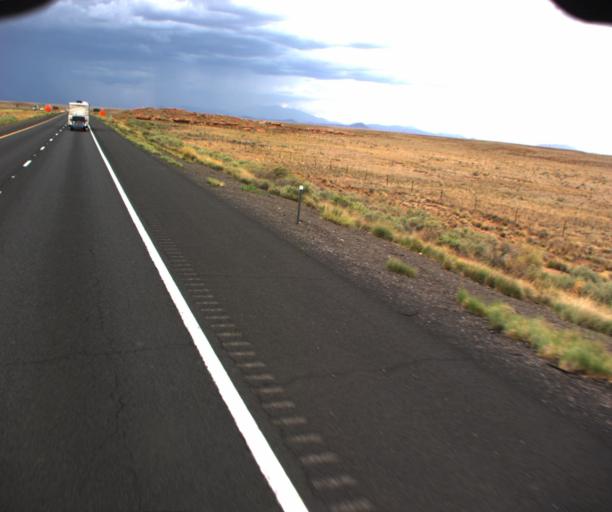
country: US
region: Arizona
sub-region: Coconino County
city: LeChee
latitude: 35.1137
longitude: -111.0618
